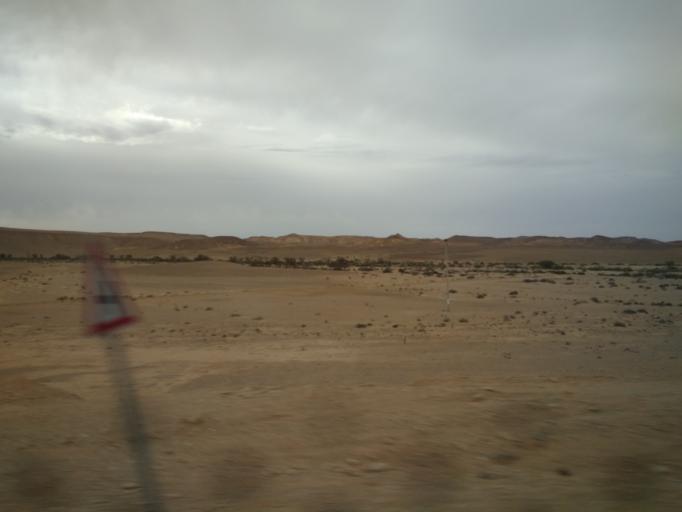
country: IL
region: Southern District
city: Eilat
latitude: 29.8655
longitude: 34.8500
